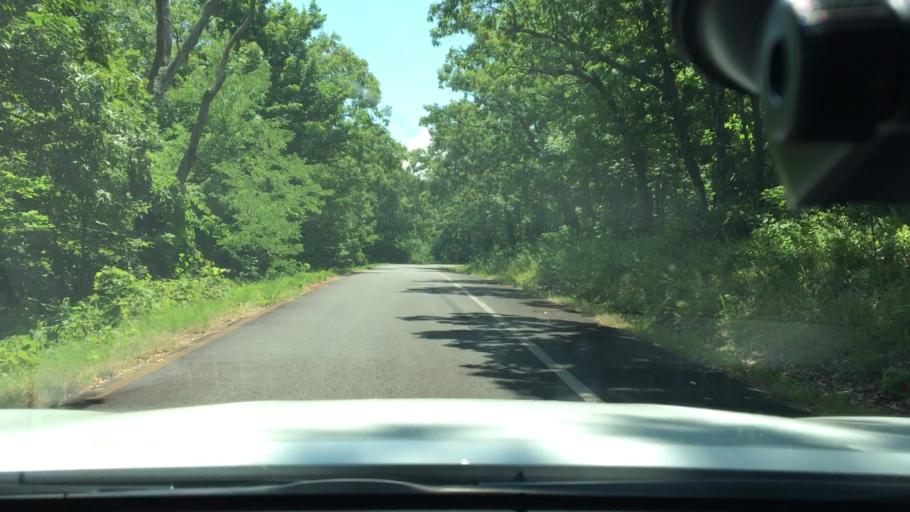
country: US
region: Arkansas
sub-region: Logan County
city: Paris
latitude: 35.1746
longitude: -93.6424
